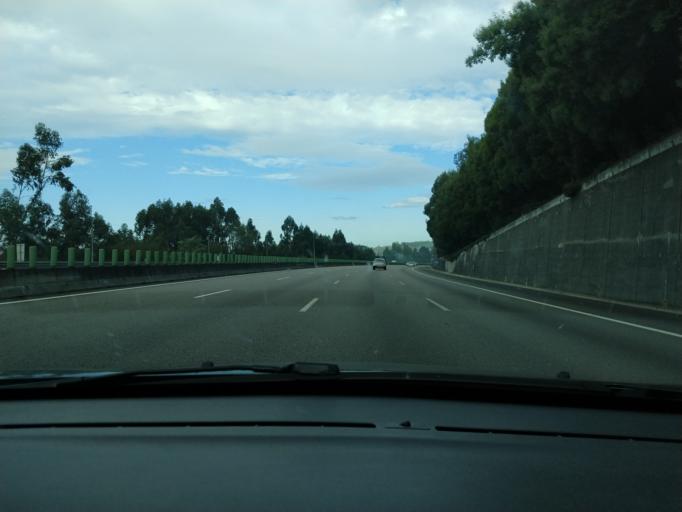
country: PT
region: Porto
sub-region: Vila Nova de Gaia
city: Perozinho
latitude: 41.0544
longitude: -8.5758
